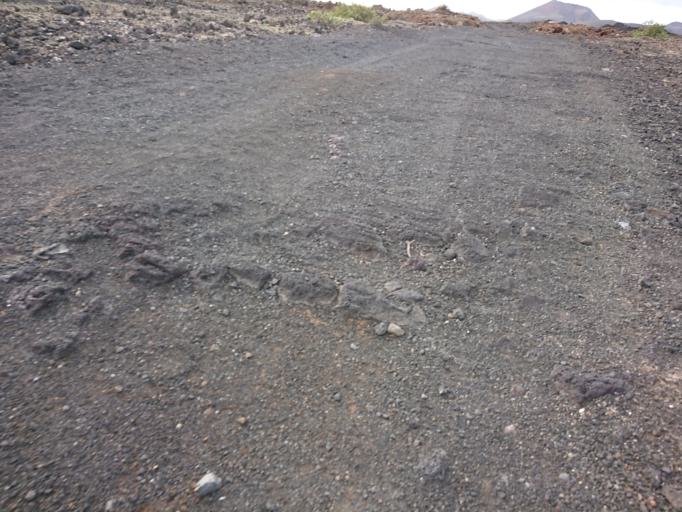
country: ES
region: Canary Islands
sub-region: Provincia de Las Palmas
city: Tias
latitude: 29.0017
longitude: -13.6880
